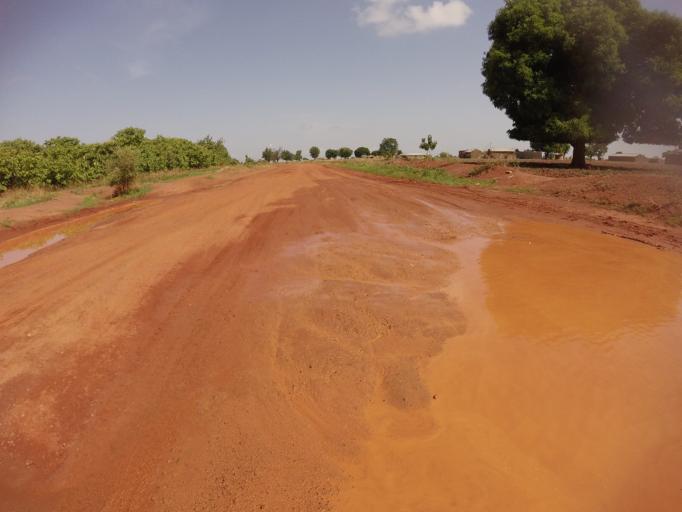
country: GH
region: Upper East
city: Bawku
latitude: 11.0075
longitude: -0.2007
